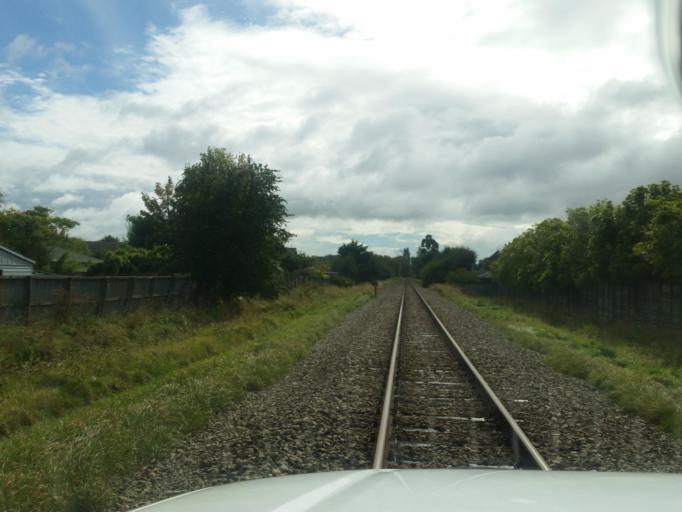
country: NZ
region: Canterbury
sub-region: Christchurch City
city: Christchurch
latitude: -43.4786
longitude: 172.6096
